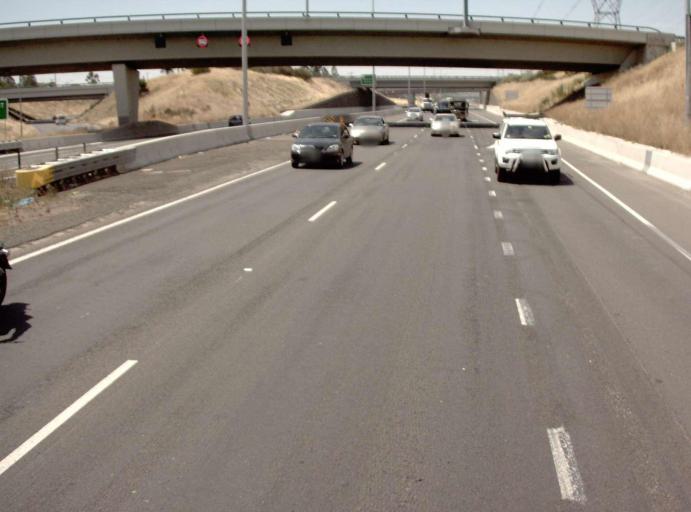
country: AU
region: Victoria
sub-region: Moonee Valley
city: Keilor East
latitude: -37.7294
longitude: 144.8577
